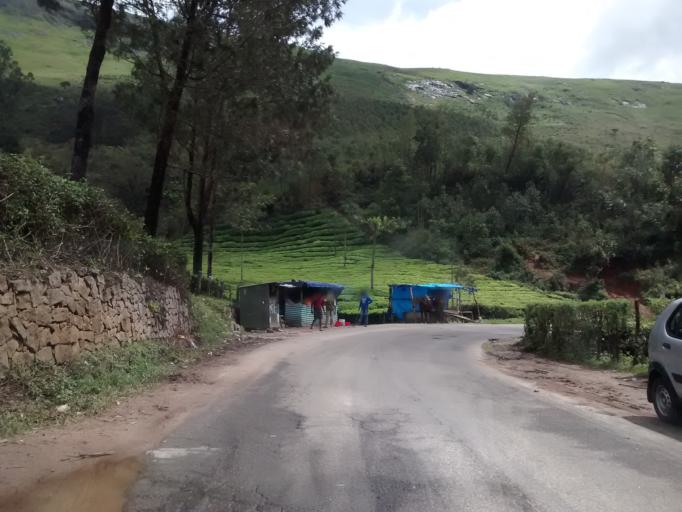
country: IN
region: Kerala
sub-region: Idukki
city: Munnar
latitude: 10.0968
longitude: 77.1014
